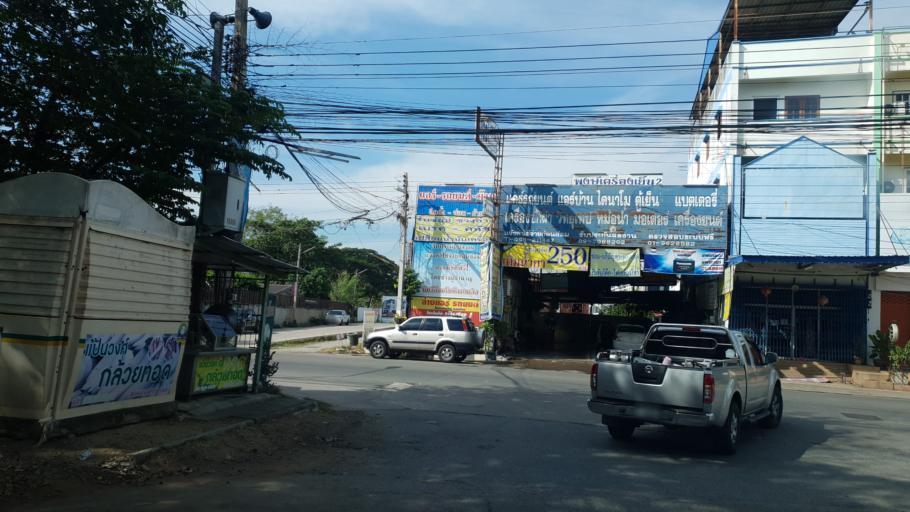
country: TH
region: Phitsanulok
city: Phitsanulok
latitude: 16.8065
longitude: 100.2678
